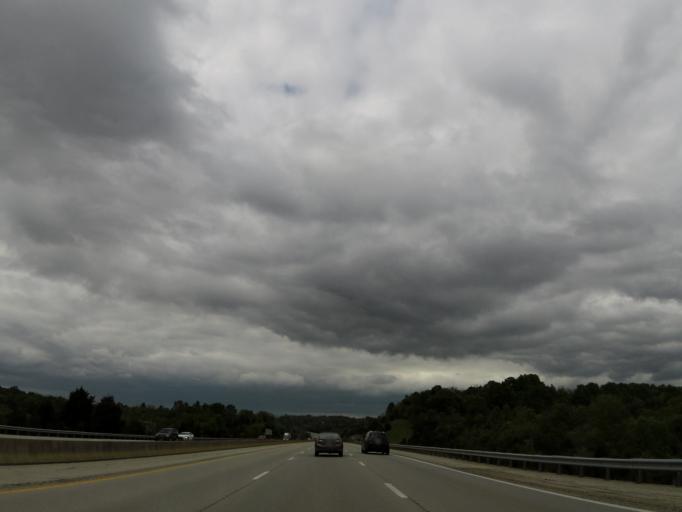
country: US
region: Kentucky
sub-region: Scott County
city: Georgetown
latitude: 38.3949
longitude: -84.5761
